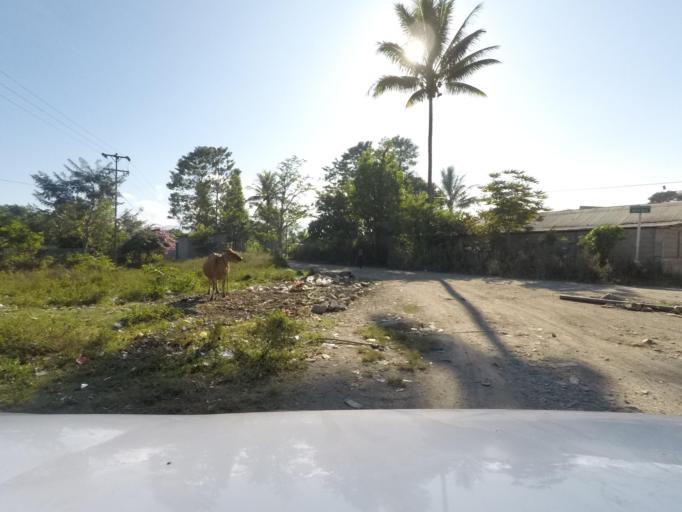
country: TL
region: Ermera
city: Gleno
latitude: -8.7281
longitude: 125.4300
